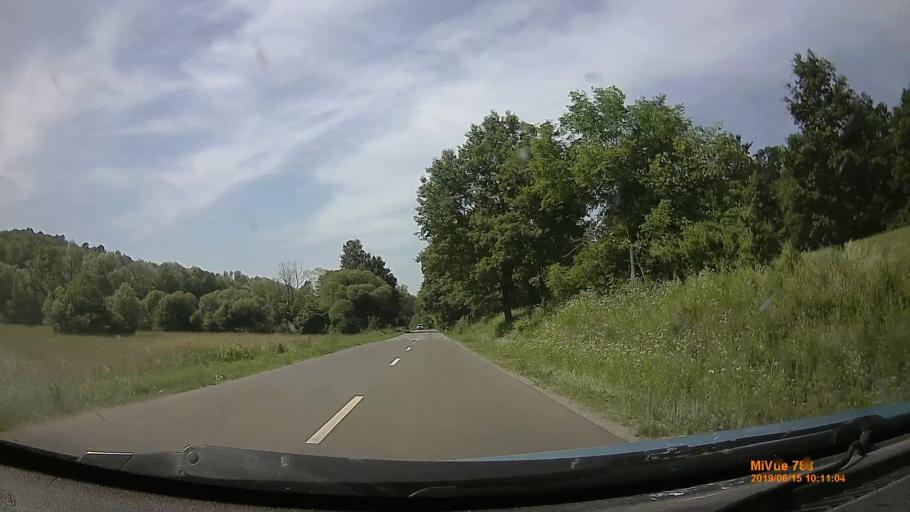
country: HU
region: Baranya
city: Buekkoesd
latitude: 46.1503
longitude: 18.0638
